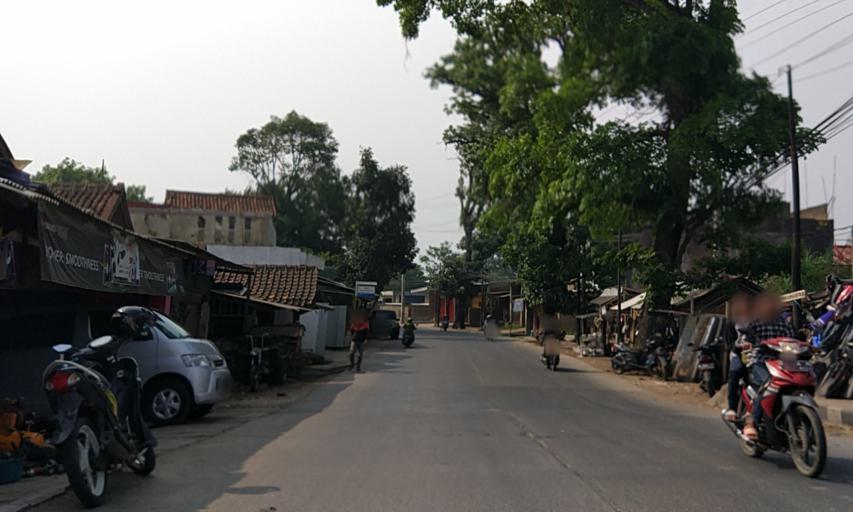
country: ID
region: West Java
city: Soreang
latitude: -7.0220
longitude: 107.5493
